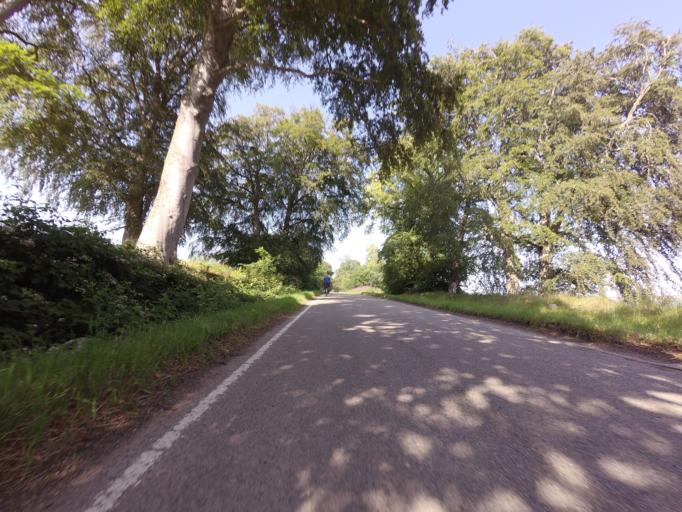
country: GB
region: Scotland
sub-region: Highland
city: Evanton
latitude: 57.6424
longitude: -4.3574
